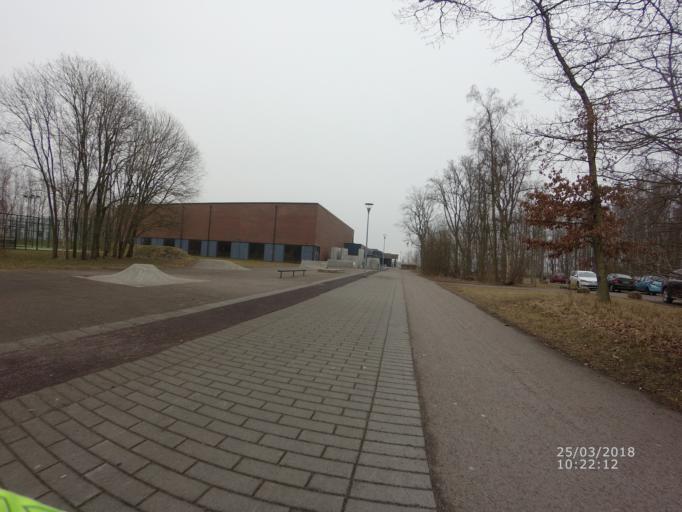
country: SE
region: Skane
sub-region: Hoganas Kommun
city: Hoganas
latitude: 56.1864
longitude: 12.5651
